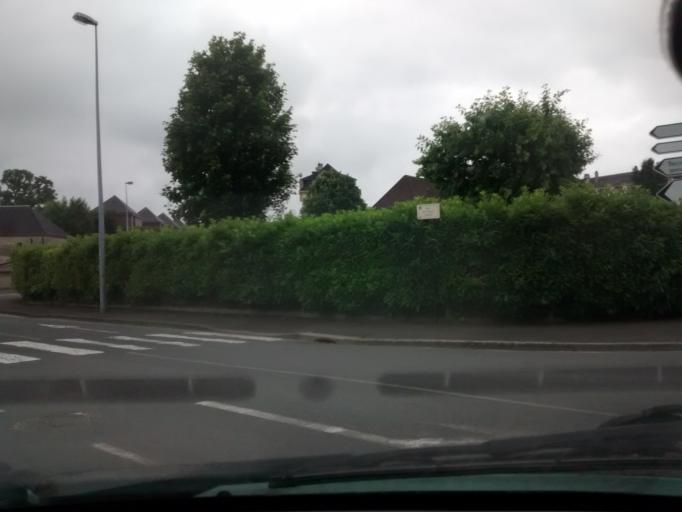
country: FR
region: Lower Normandy
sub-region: Departement de la Manche
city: Agneaux
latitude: 49.1095
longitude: -1.1048
